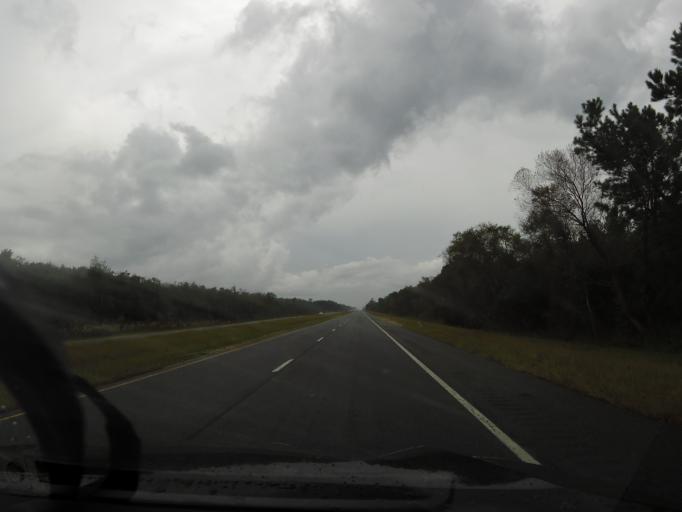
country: US
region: Georgia
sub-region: Wayne County
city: Jesup
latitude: 31.4440
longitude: -81.6901
